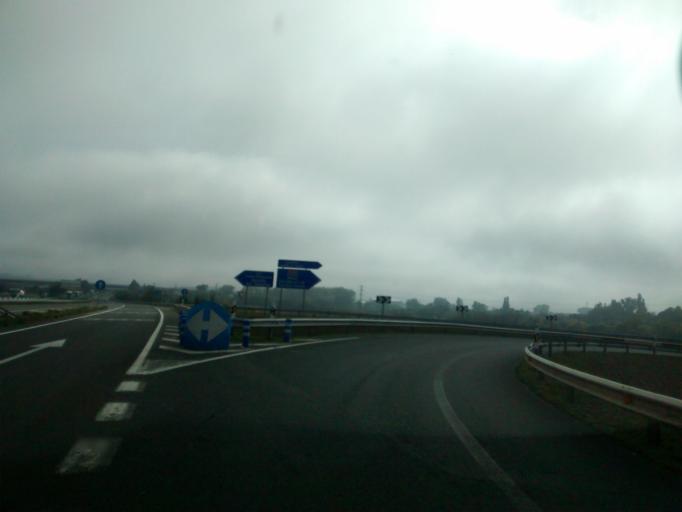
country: ES
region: Basque Country
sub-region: Provincia de Alava
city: Gasteiz / Vitoria
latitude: 42.8807
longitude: -2.6554
